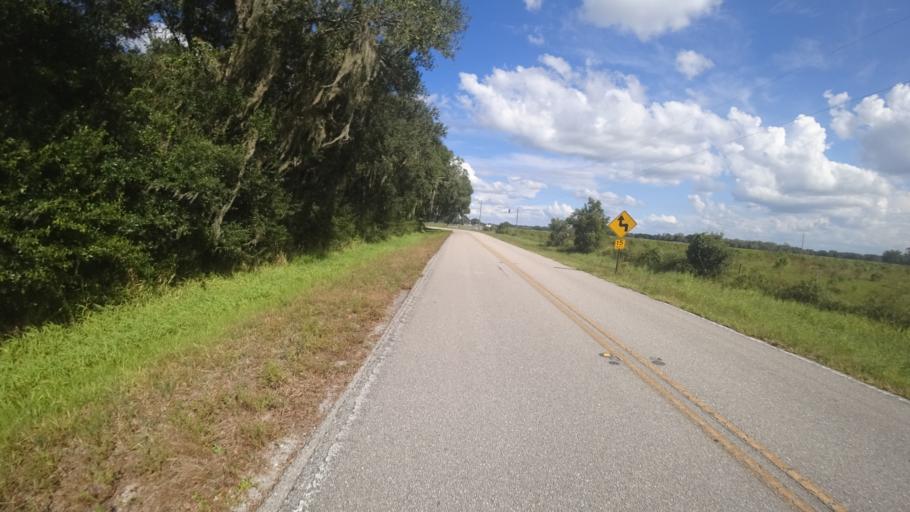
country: US
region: Florida
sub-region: DeSoto County
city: Nocatee
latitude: 27.2718
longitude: -82.0779
